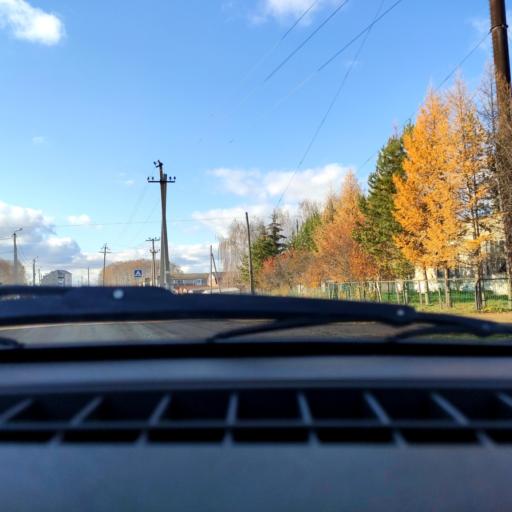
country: RU
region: Bashkortostan
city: Mikhaylovka
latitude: 54.7812
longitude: 55.8410
